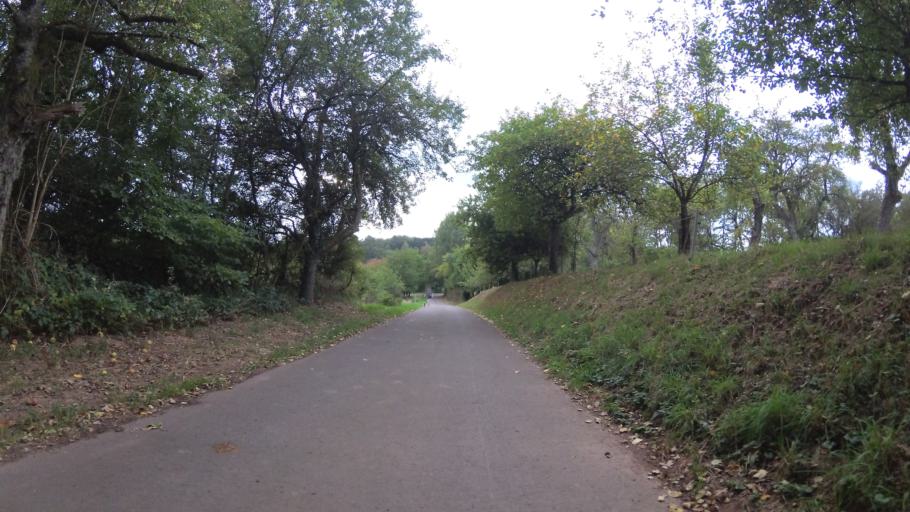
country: DE
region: Saarland
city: Ottweiler
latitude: 49.4136
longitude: 7.1441
